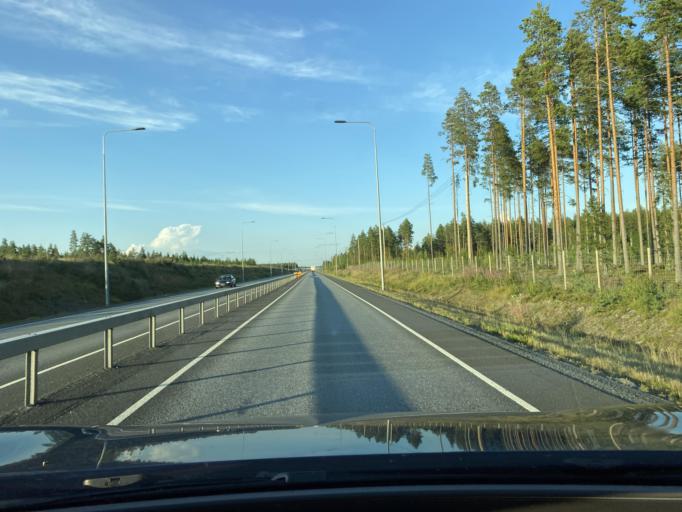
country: FI
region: Southern Ostrobothnia
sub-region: Seinaejoki
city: Seinaejoki
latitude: 62.7146
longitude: 22.8529
